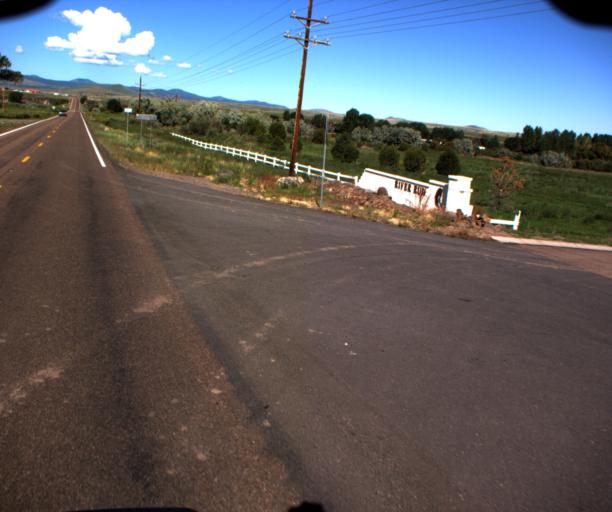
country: US
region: Arizona
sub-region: Apache County
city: Eagar
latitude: 34.1109
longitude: -109.3106
